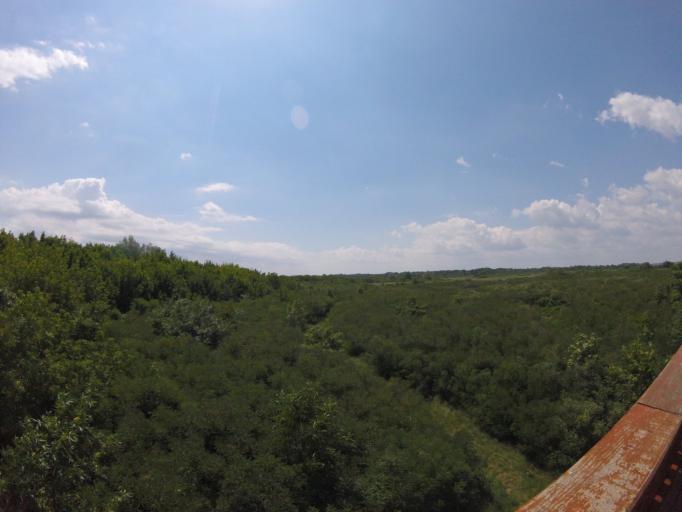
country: HU
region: Jasz-Nagykun-Szolnok
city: Tiszaszolos
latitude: 47.5839
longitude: 20.6715
